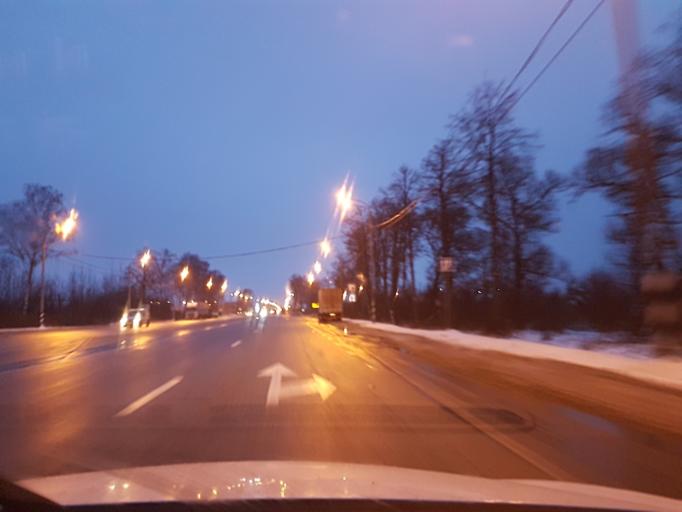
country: RU
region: Moskovskaya
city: Spas-Zaulok
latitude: 56.4898
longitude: 36.5624
